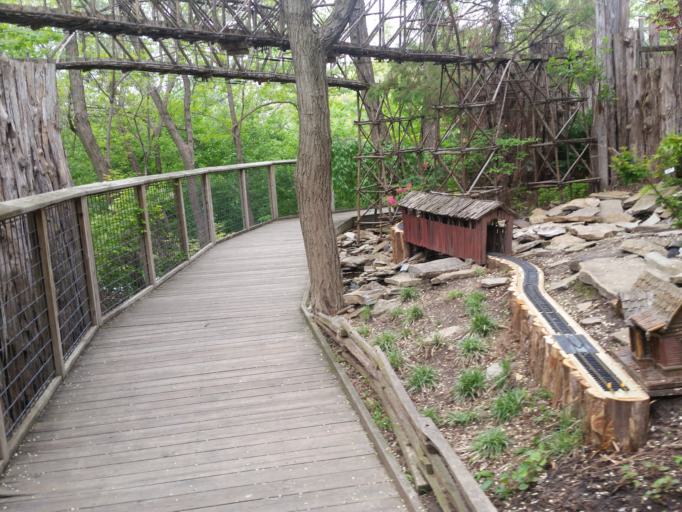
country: US
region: Nebraska
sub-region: Douglas County
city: Omaha
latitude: 41.2389
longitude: -95.9182
